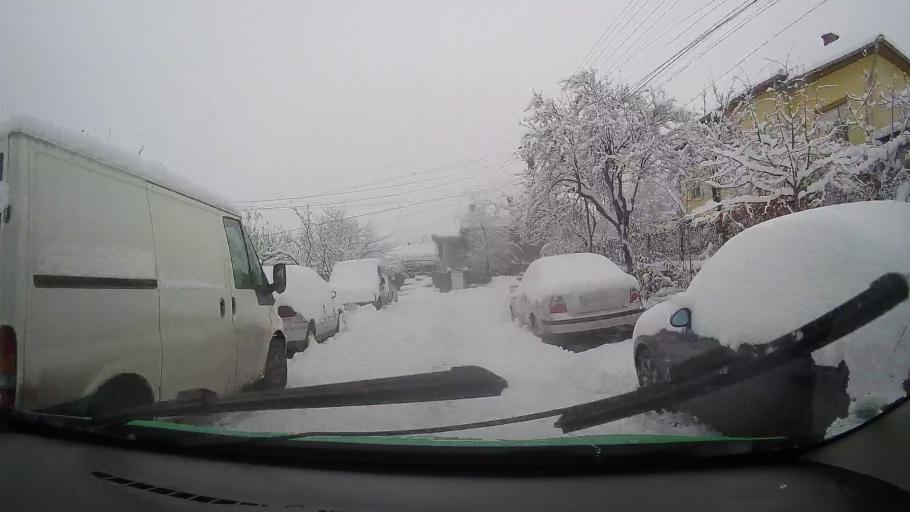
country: RO
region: Hunedoara
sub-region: Comuna Teliucu Inferior
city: Teliucu Inferior
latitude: 45.7000
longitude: 22.8941
